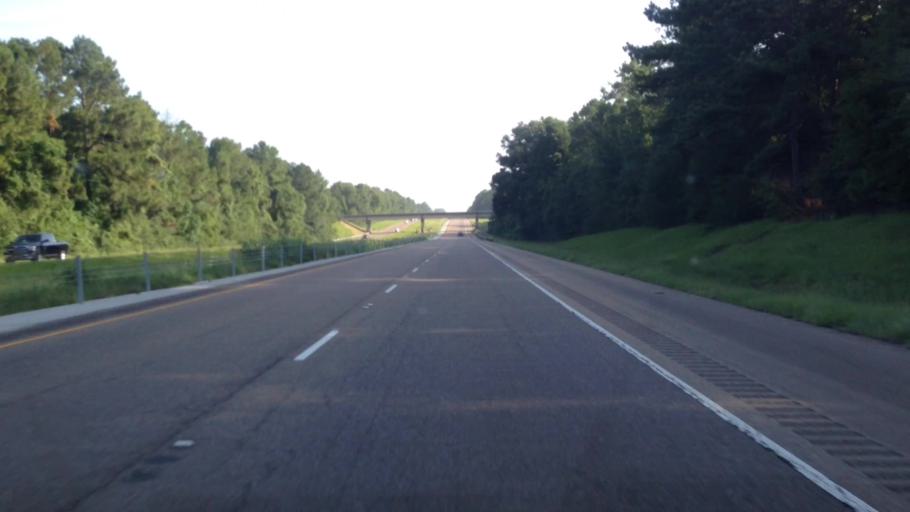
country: US
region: Louisiana
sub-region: Tangipahoa Parish
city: Roseland
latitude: 30.7593
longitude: -90.5328
